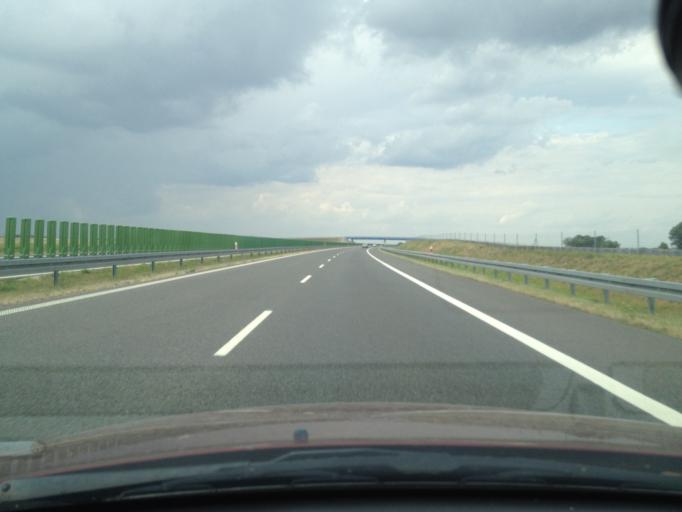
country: PL
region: West Pomeranian Voivodeship
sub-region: Powiat pyrzycki
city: Kozielice
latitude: 53.1031
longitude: 14.7735
